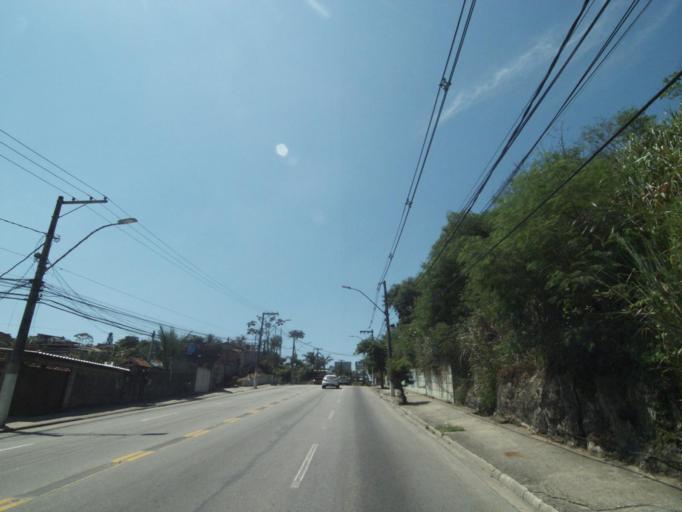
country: BR
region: Rio de Janeiro
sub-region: Niteroi
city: Niteroi
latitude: -22.9095
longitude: -43.0695
